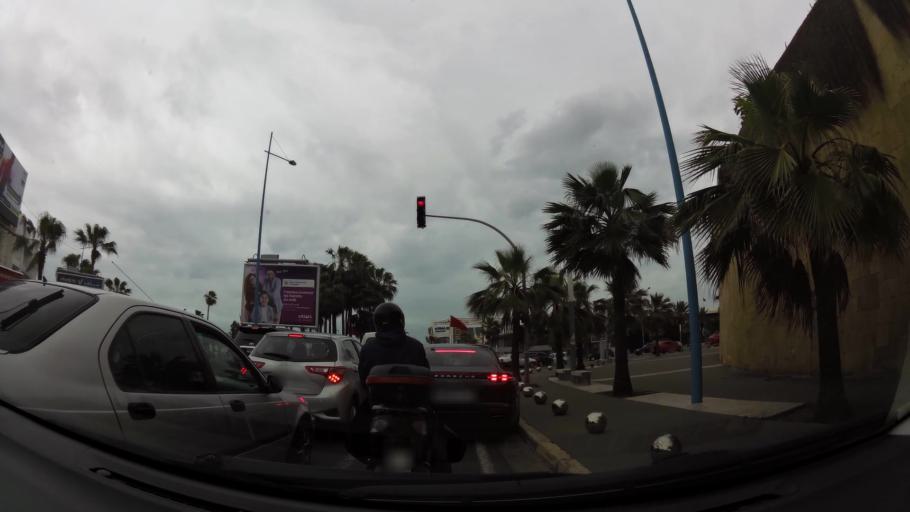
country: MA
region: Grand Casablanca
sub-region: Casablanca
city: Casablanca
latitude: 33.5950
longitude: -7.6678
